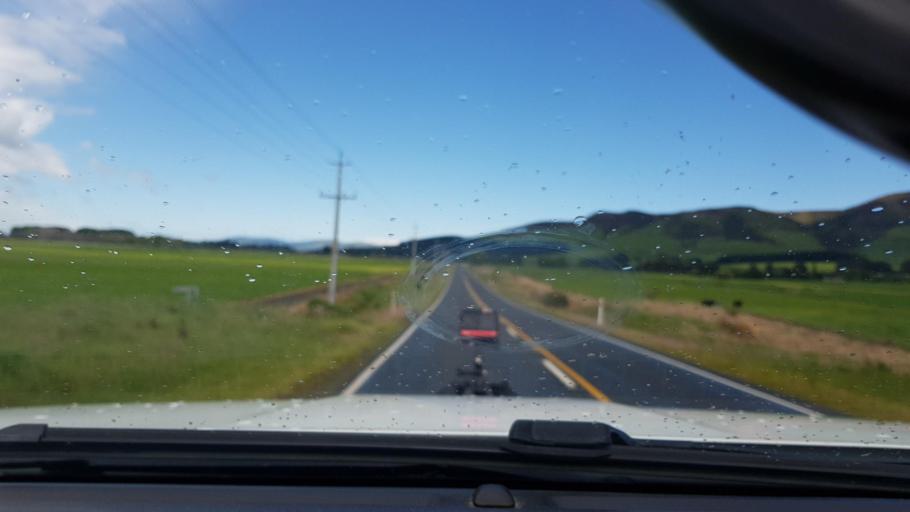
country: NZ
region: Southland
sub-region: Southland District
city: Winton
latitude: -45.7913
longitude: 168.3861
